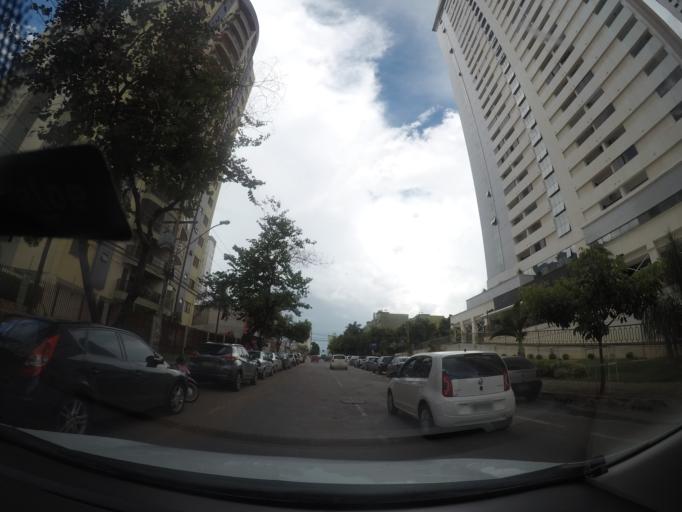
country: BR
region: Goias
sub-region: Goiania
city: Goiania
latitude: -16.7191
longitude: -49.2652
